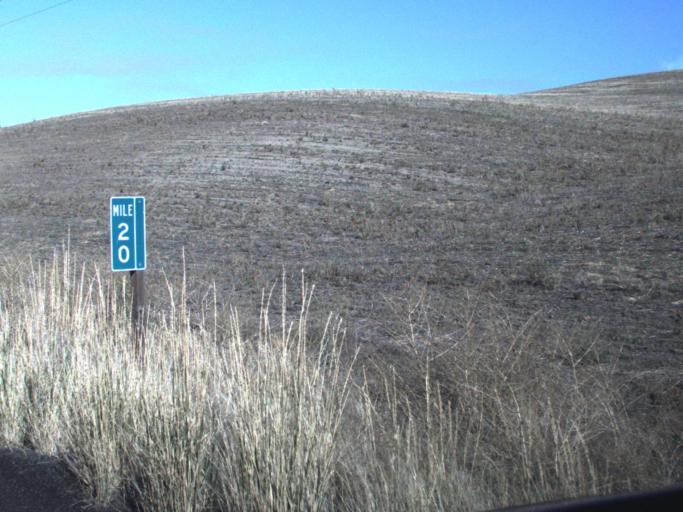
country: US
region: Washington
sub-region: Walla Walla County
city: Walla Walla
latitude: 46.2491
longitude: -118.3617
